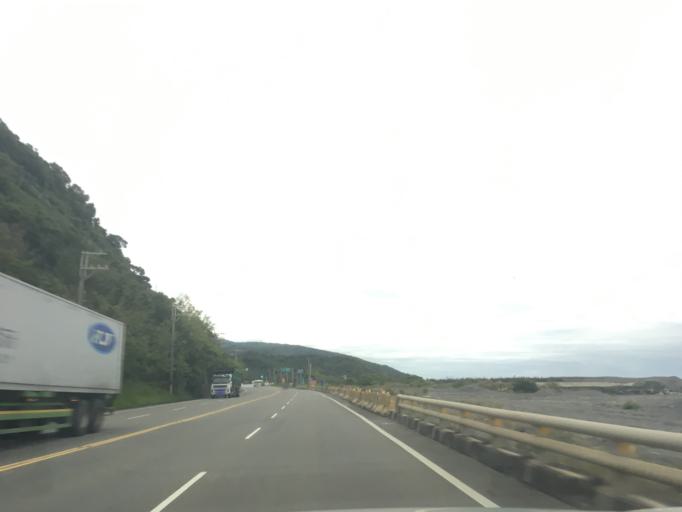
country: TW
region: Taiwan
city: Hengchun
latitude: 22.3332
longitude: 120.8937
